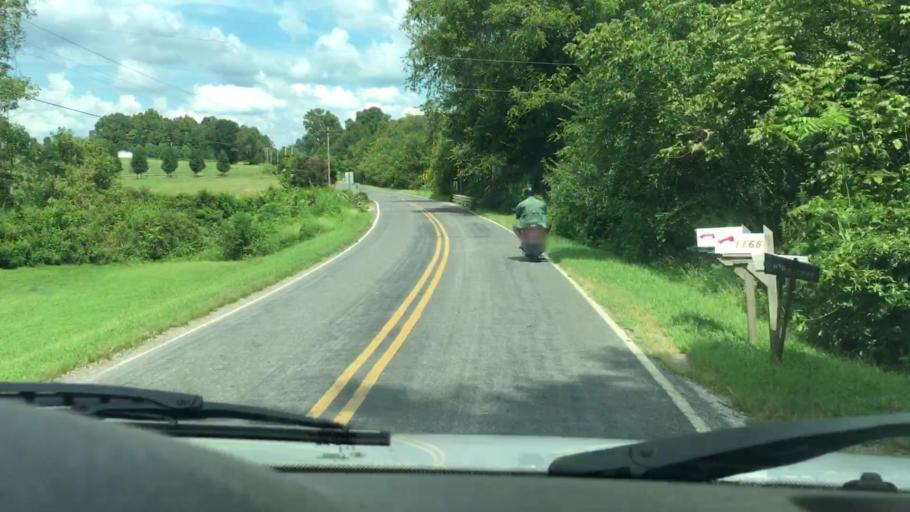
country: US
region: North Carolina
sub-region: Iredell County
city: Mooresville
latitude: 35.6700
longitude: -80.7840
